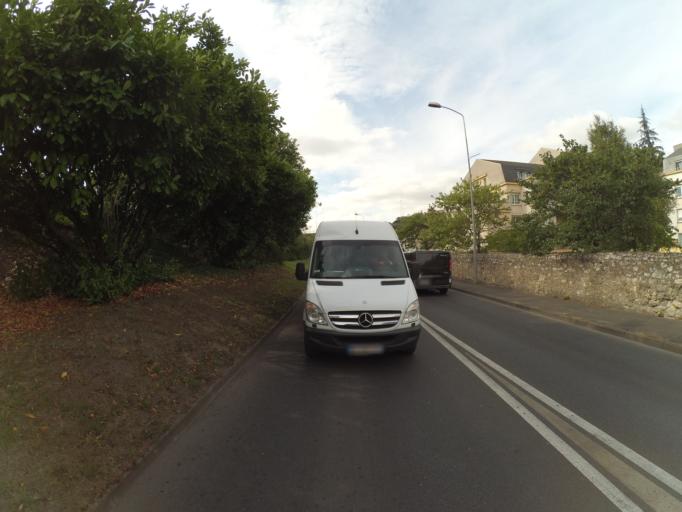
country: FR
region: Centre
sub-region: Departement d'Indre-et-Loire
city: Tours
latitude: 47.4032
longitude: 0.7040
